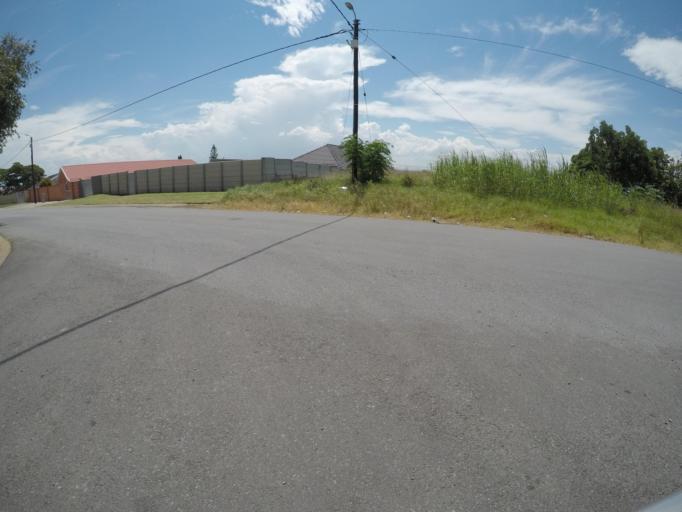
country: ZA
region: Eastern Cape
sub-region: Buffalo City Metropolitan Municipality
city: East London
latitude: -33.0322
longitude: 27.8527
